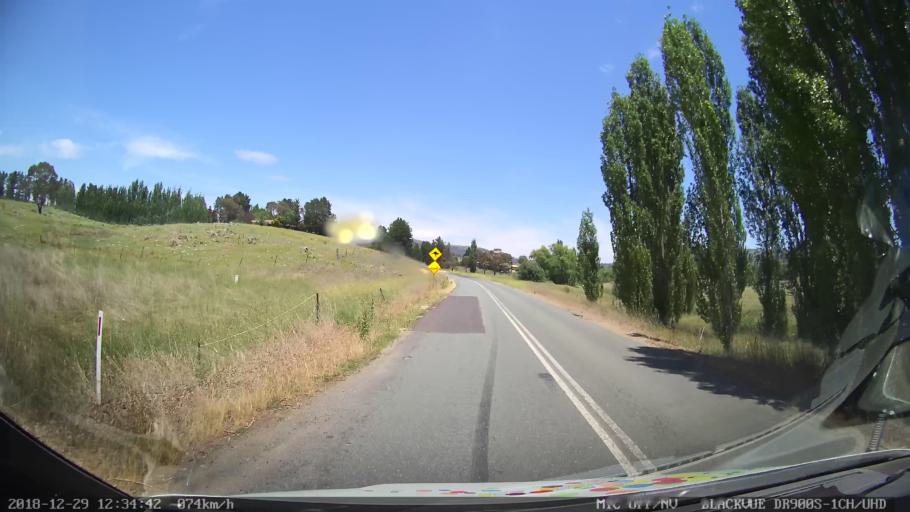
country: AU
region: Australian Capital Territory
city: Macarthur
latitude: -35.5547
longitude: 149.2245
